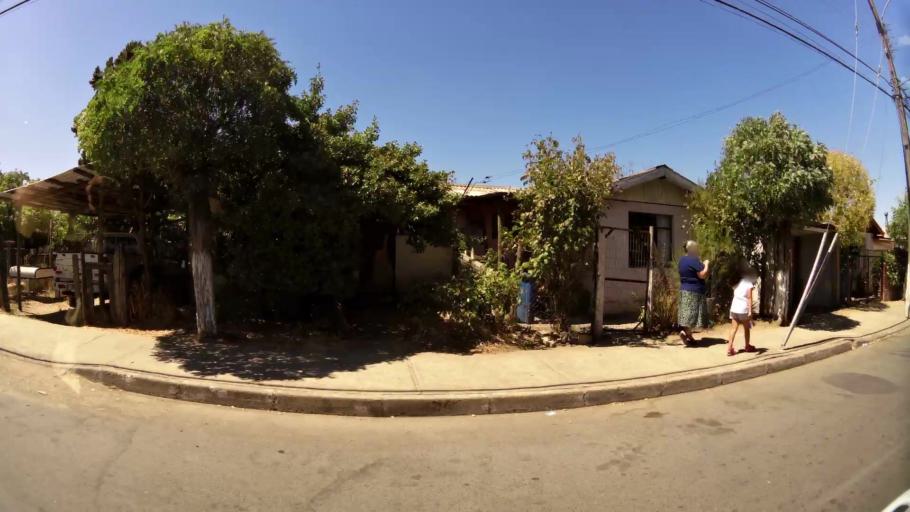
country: CL
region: Maule
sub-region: Provincia de Talca
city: Talca
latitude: -35.3058
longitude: -71.5140
